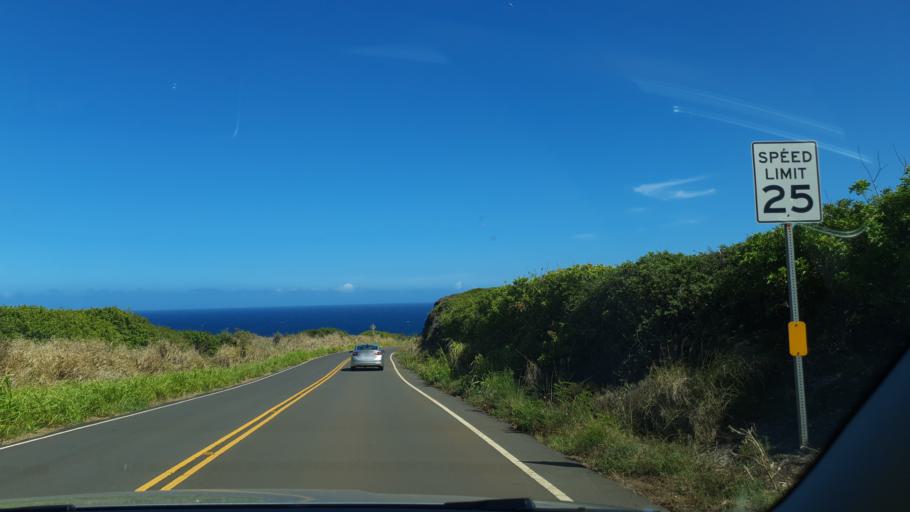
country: US
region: Hawaii
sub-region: Maui County
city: Napili-Honokowai
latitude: 21.0143
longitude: -156.5726
